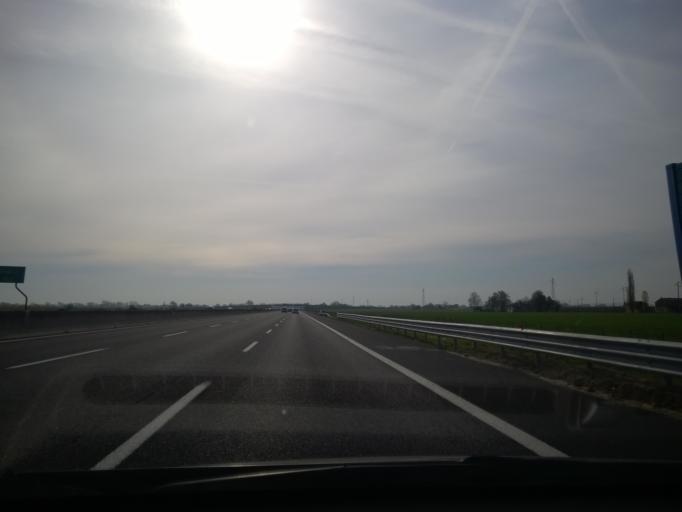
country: IT
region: Emilia-Romagna
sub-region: Provincia di Ravenna
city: Granarolo
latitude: 44.2952
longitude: 11.9761
